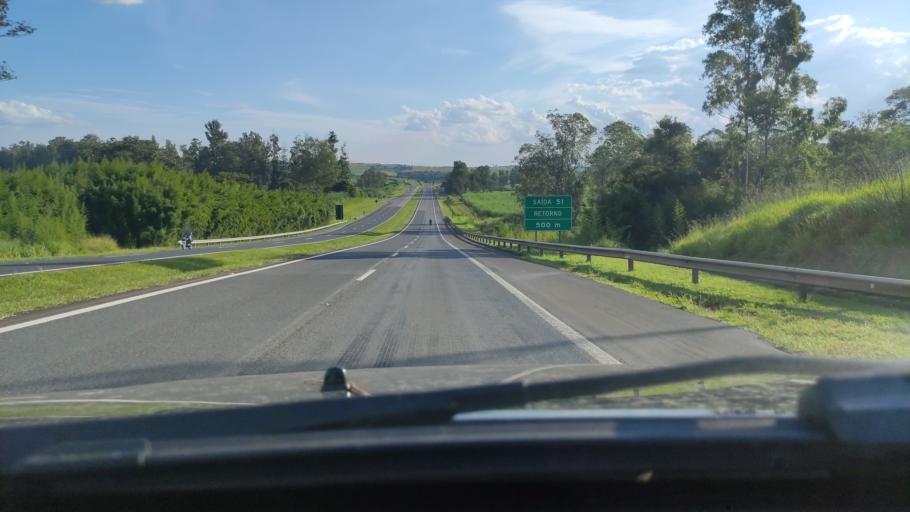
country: BR
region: Sao Paulo
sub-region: Itapira
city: Itapira
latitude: -22.4498
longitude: -46.8885
